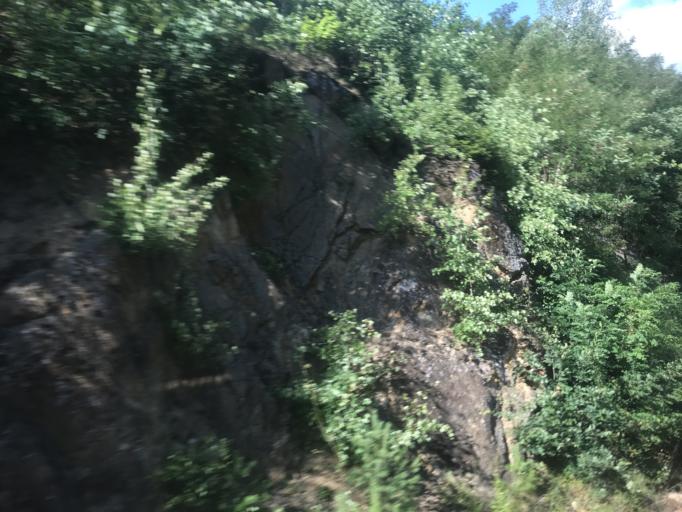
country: AT
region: Upper Austria
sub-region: Politischer Bezirk Freistadt
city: Freistadt
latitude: 48.4619
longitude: 14.5137
